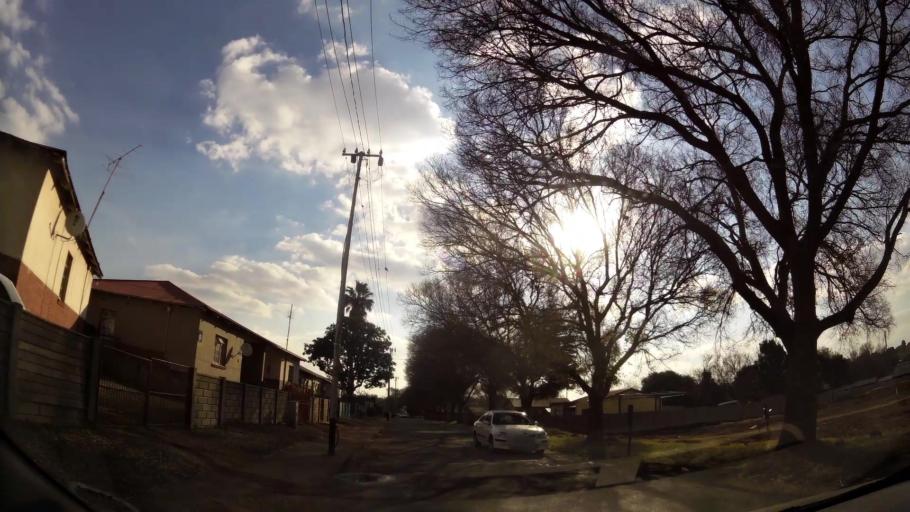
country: ZA
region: Gauteng
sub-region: West Rand District Municipality
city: Krugersdorp
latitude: -26.0958
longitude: 27.7580
